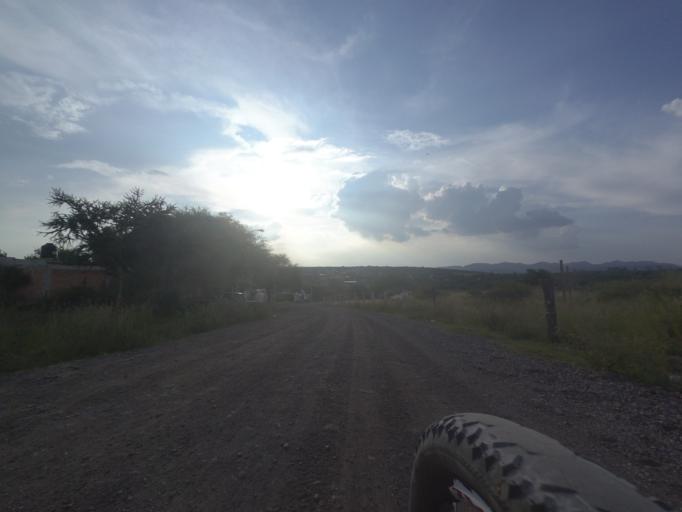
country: MX
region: Aguascalientes
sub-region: Aguascalientes
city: Los Canos
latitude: 21.7763
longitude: -102.3717
